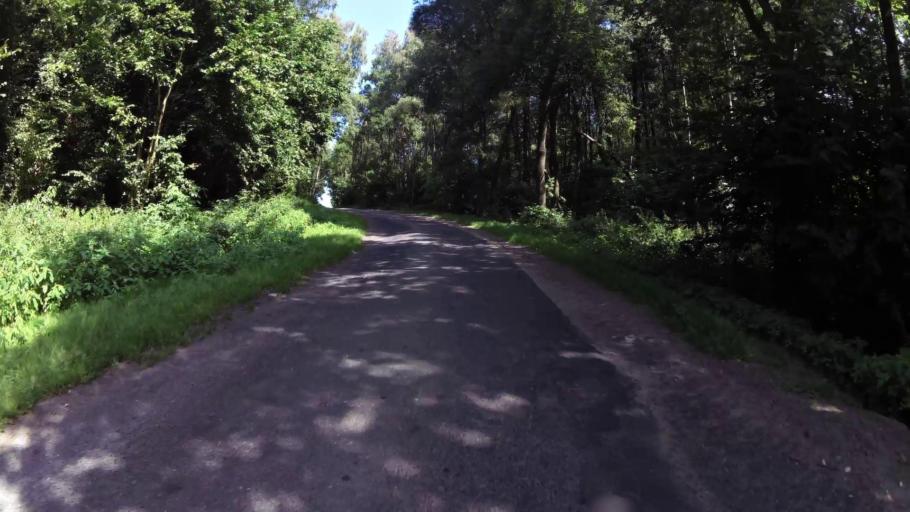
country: PL
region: West Pomeranian Voivodeship
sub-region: Powiat choszczenski
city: Choszczno
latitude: 53.2523
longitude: 15.4240
